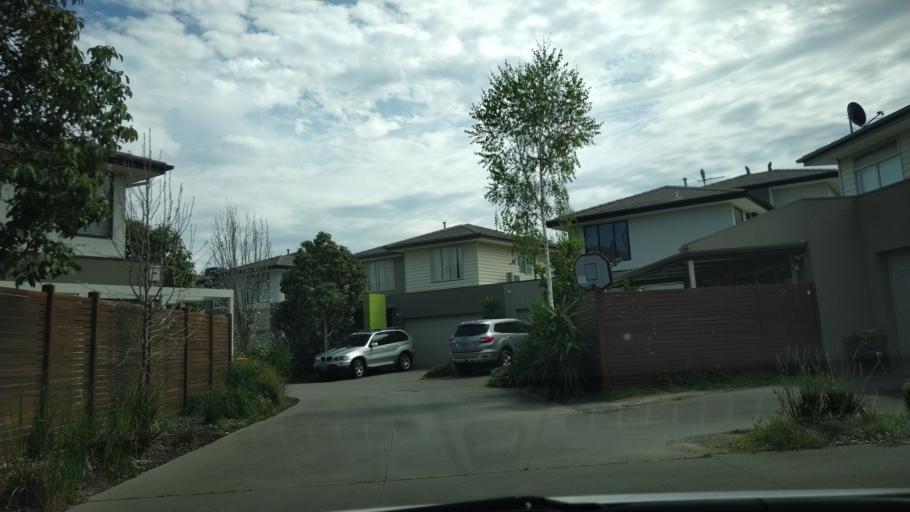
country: AU
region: Victoria
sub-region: Greater Dandenong
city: Keysborough
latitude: -38.0041
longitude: 145.1594
